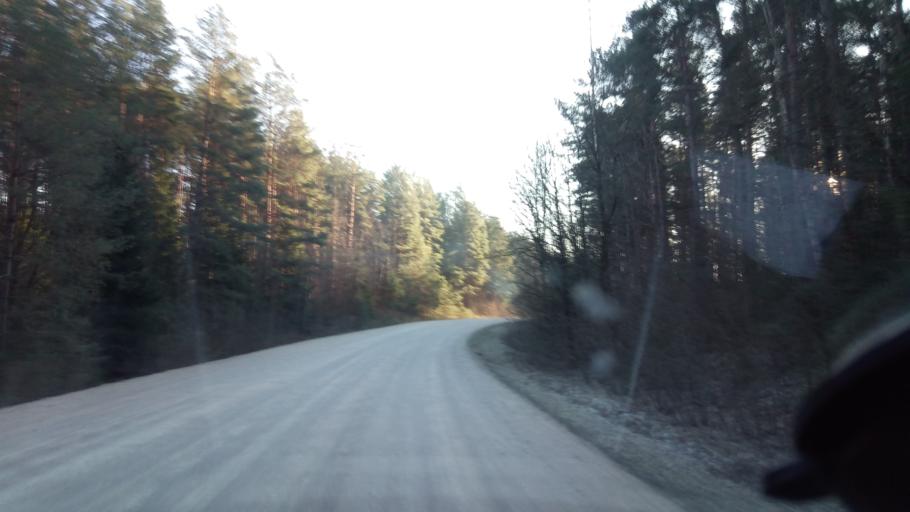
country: LT
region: Alytaus apskritis
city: Druskininkai
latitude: 54.1446
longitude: 23.9477
